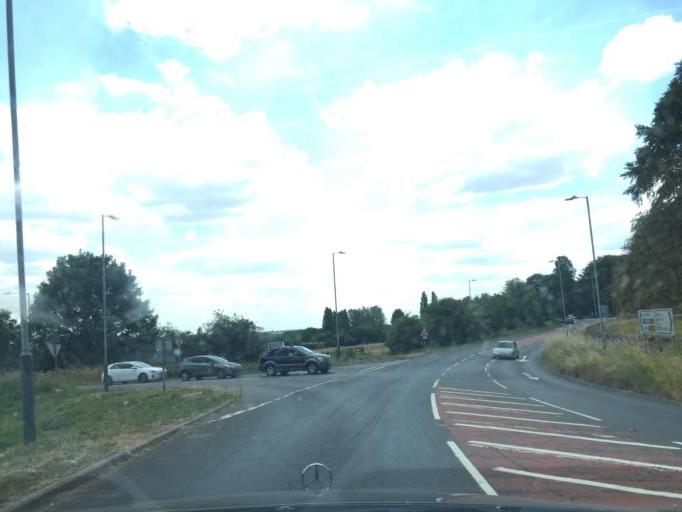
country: GB
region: England
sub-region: Warwickshire
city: Bedworth
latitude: 52.4498
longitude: -1.4098
